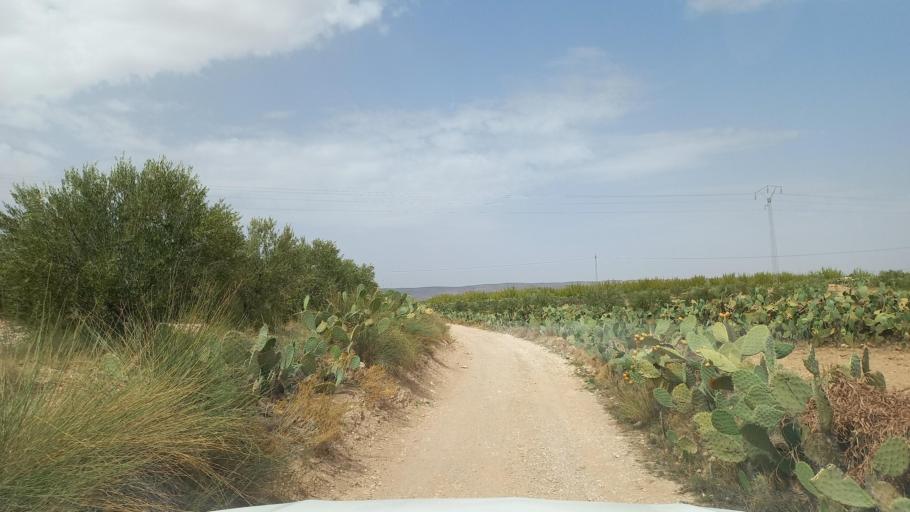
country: TN
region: Al Qasrayn
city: Kasserine
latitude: 35.2846
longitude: 9.0092
